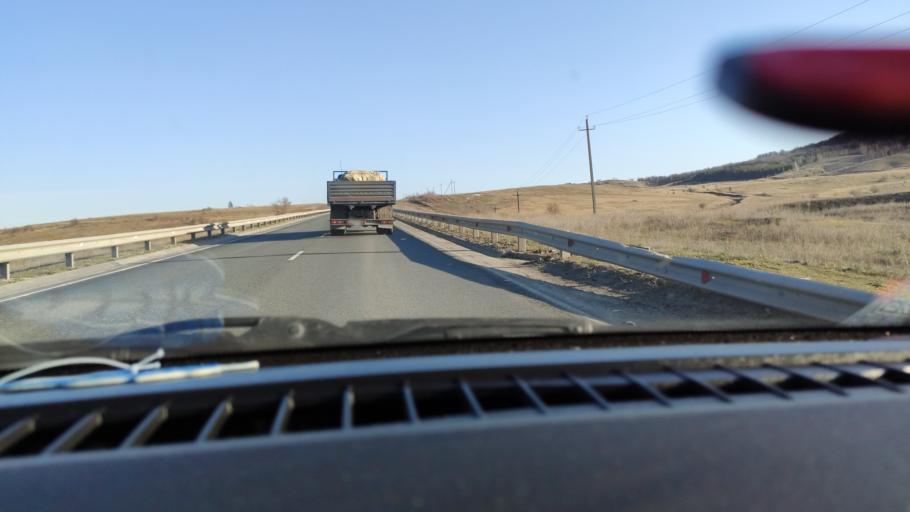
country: RU
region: Saratov
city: Alekseyevka
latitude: 52.3150
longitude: 47.9234
